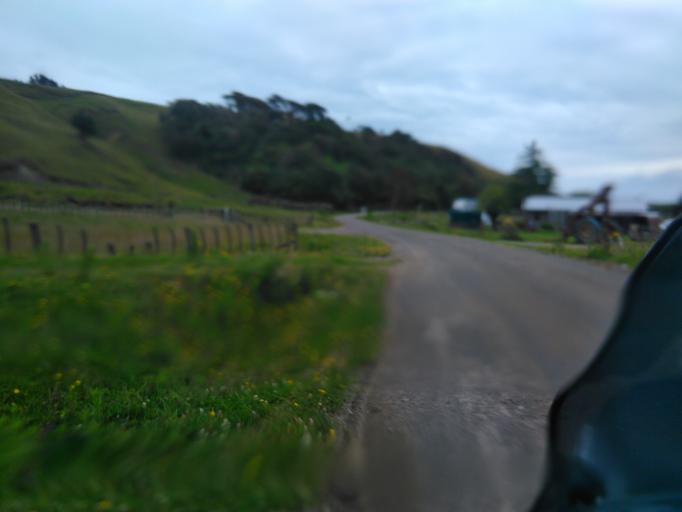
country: NZ
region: Bay of Plenty
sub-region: Opotiki District
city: Opotiki
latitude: -38.0242
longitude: 177.4370
